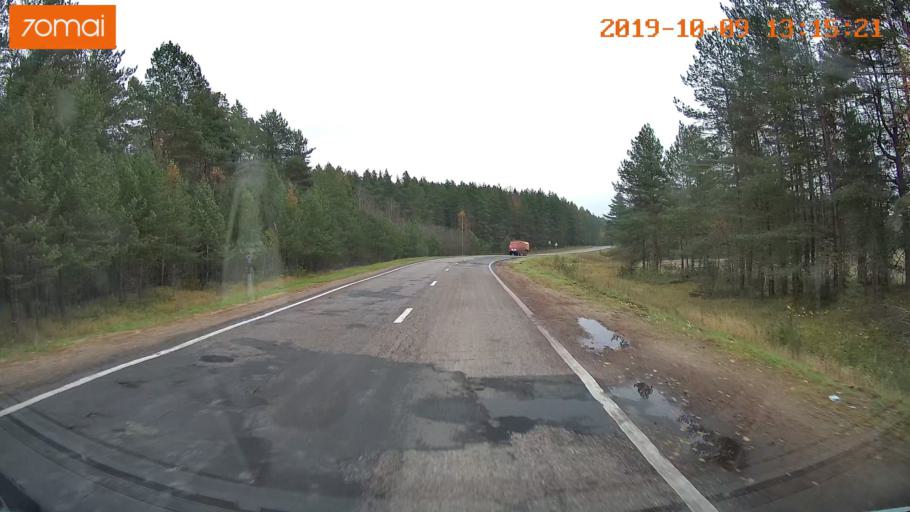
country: RU
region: Jaroslavl
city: Lyubim
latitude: 58.3677
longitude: 40.7509
